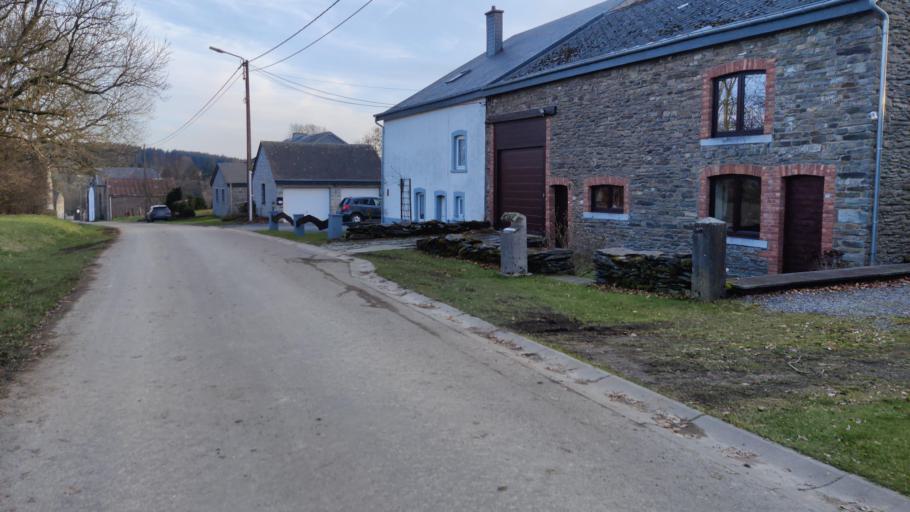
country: BE
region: Wallonia
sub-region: Province du Luxembourg
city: Houffalize
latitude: 50.1110
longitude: 5.8375
